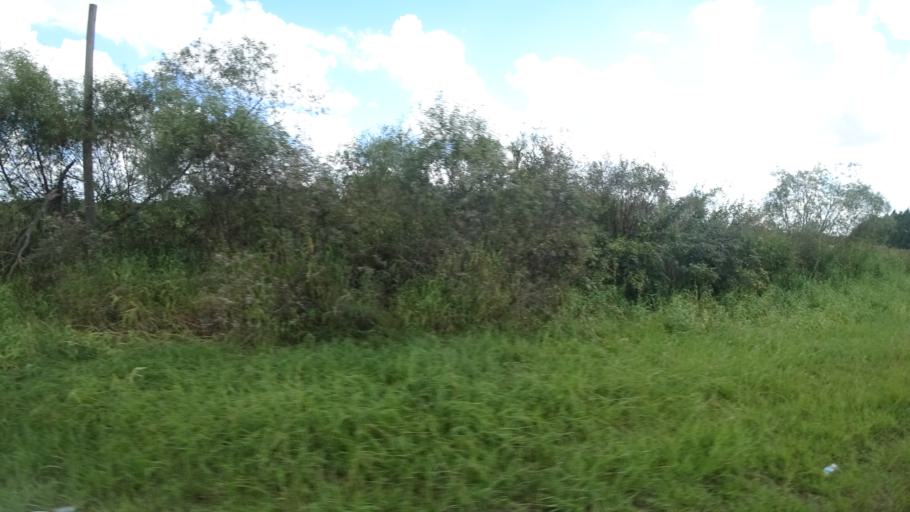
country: US
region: Florida
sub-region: DeSoto County
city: Arcadia
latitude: 27.3097
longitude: -82.1130
